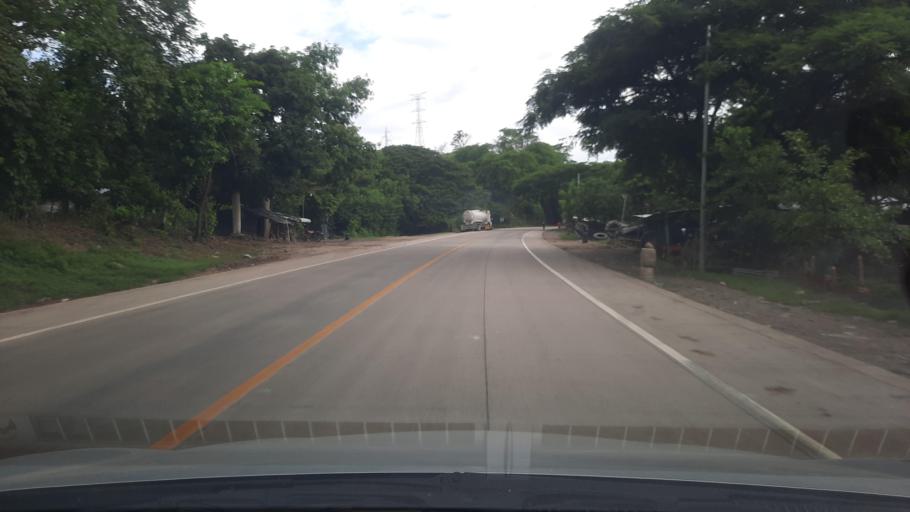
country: NI
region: Chinandega
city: Somotillo
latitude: 12.8655
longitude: -86.8512
